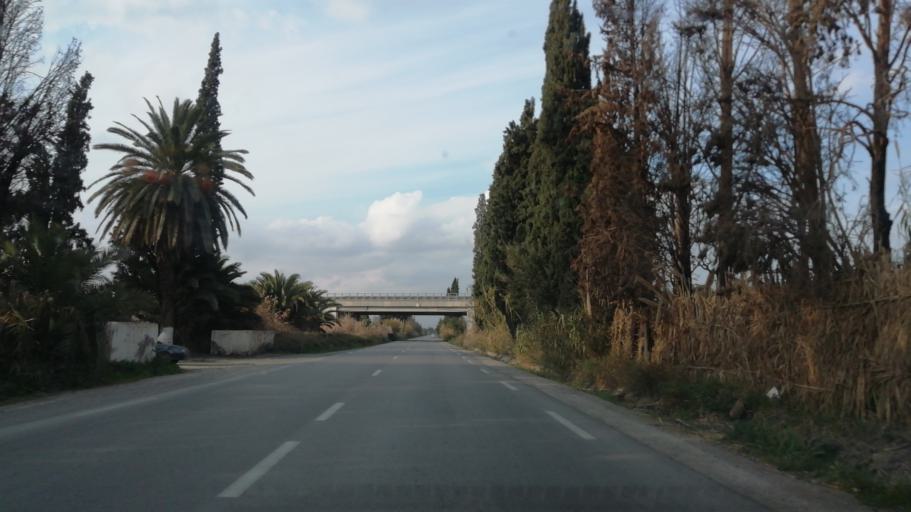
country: DZ
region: Mascara
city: Mascara
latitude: 35.6198
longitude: 0.0469
